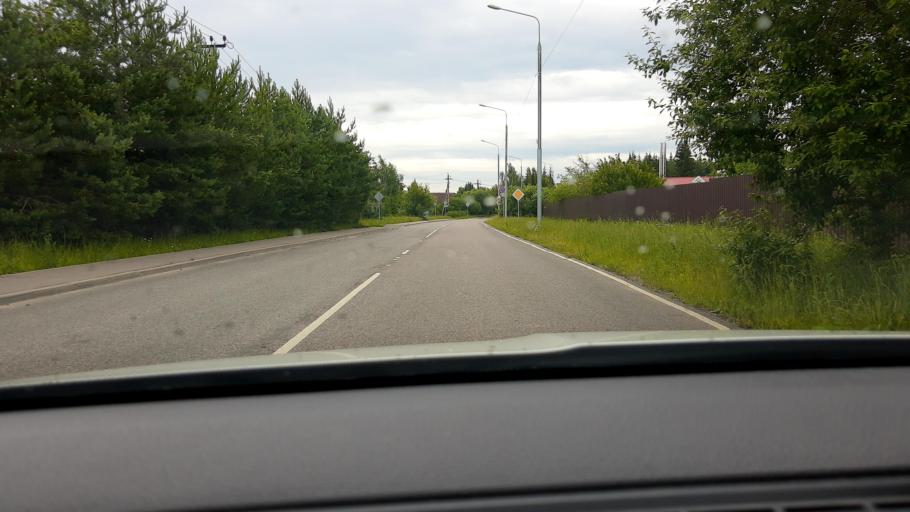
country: RU
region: Moskovskaya
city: Troitsk
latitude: 55.4899
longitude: 37.2610
